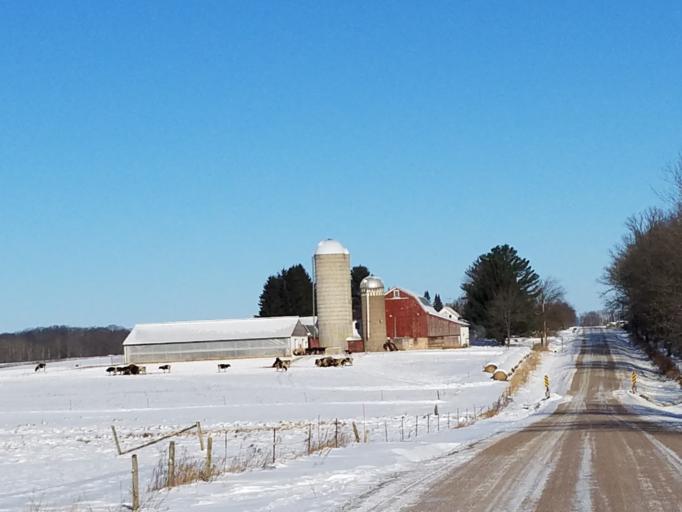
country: US
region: Wisconsin
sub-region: Clark County
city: Loyal
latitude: 44.6138
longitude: -90.3969
